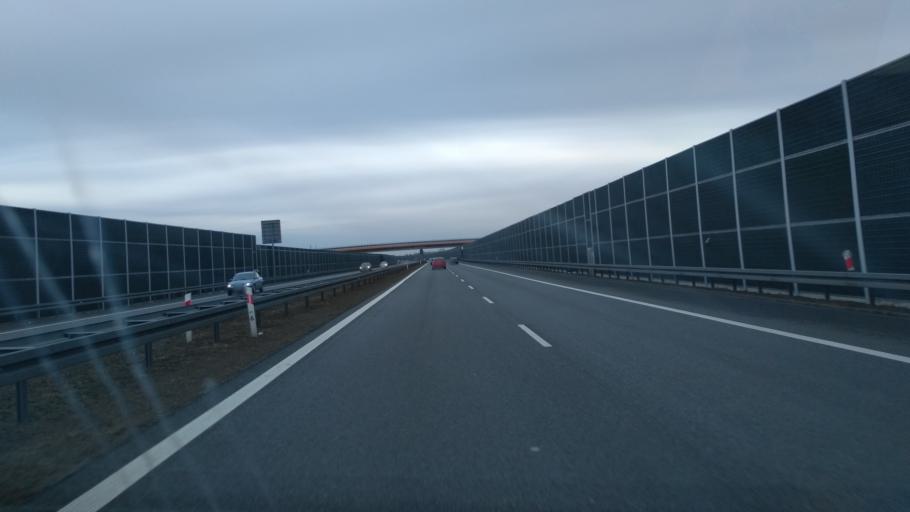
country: PL
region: Lesser Poland Voivodeship
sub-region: Powiat bochenski
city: Stanislawice
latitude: 49.9941
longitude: 20.3693
